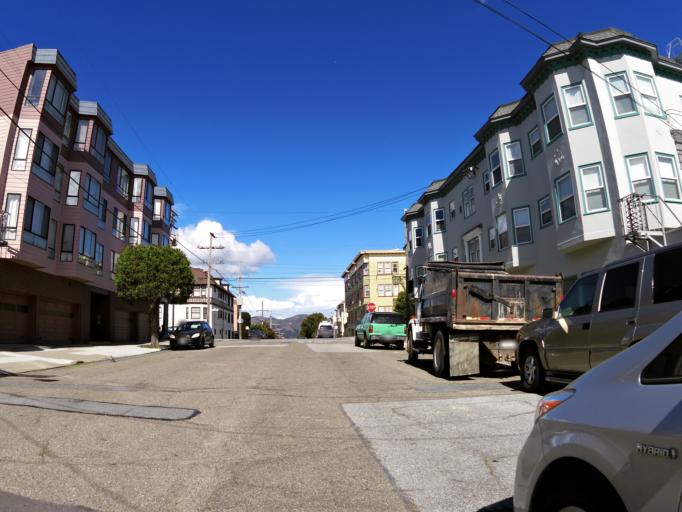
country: US
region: California
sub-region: San Francisco County
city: San Francisco
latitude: 37.7852
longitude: -122.4873
